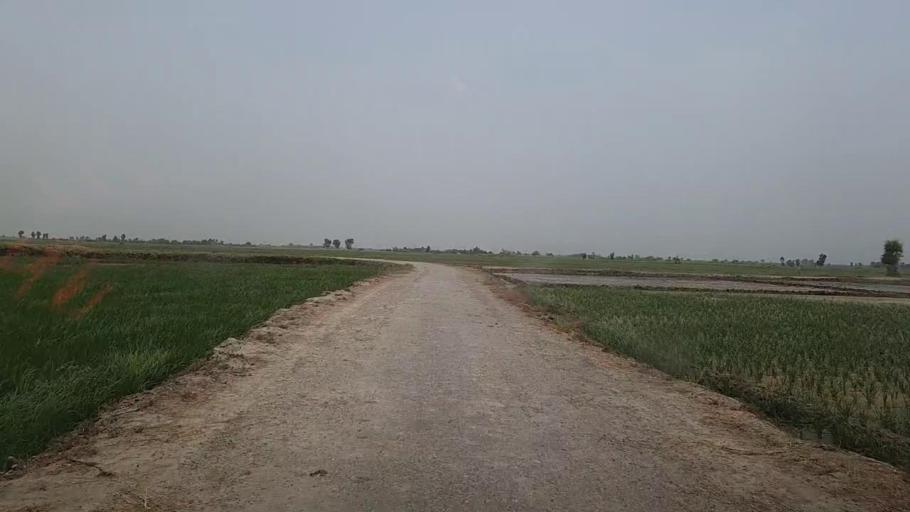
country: PK
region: Sindh
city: Sita Road
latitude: 27.0694
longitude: 67.8535
